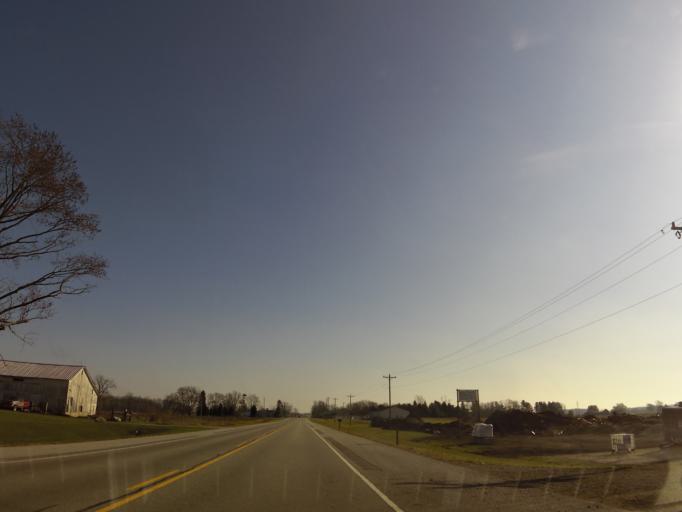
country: US
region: Indiana
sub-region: Union County
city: Liberty
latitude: 39.5922
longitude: -84.8558
